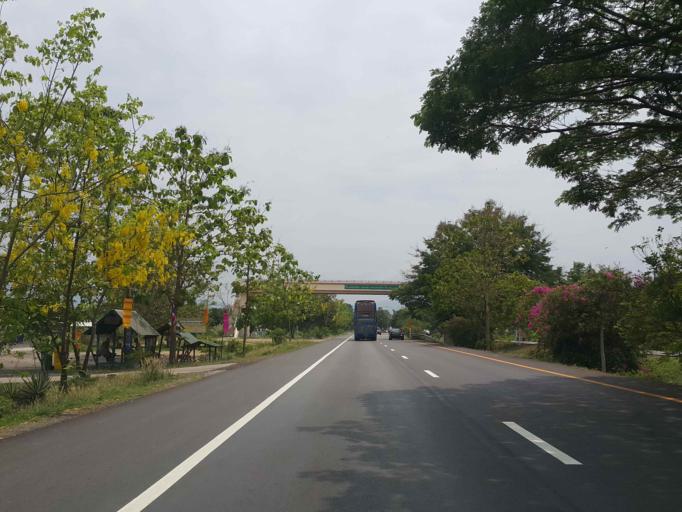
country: TH
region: Lampang
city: Sop Prap
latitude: 17.9275
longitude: 99.3465
